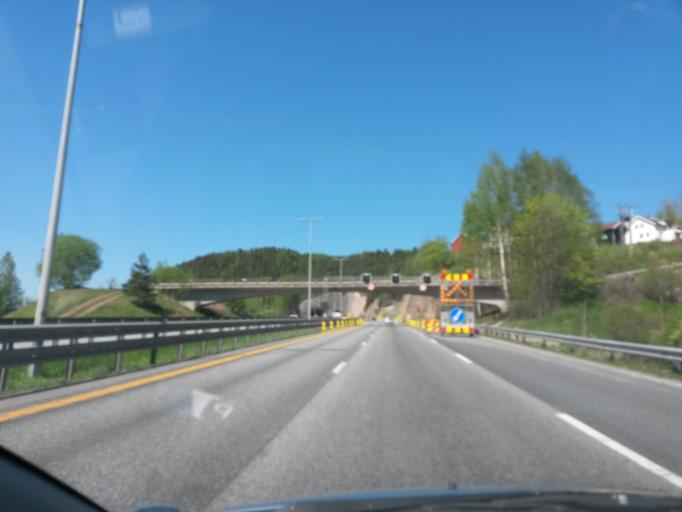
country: NO
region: Buskerud
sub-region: Lier
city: Tranby
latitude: 59.7873
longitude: 10.2731
